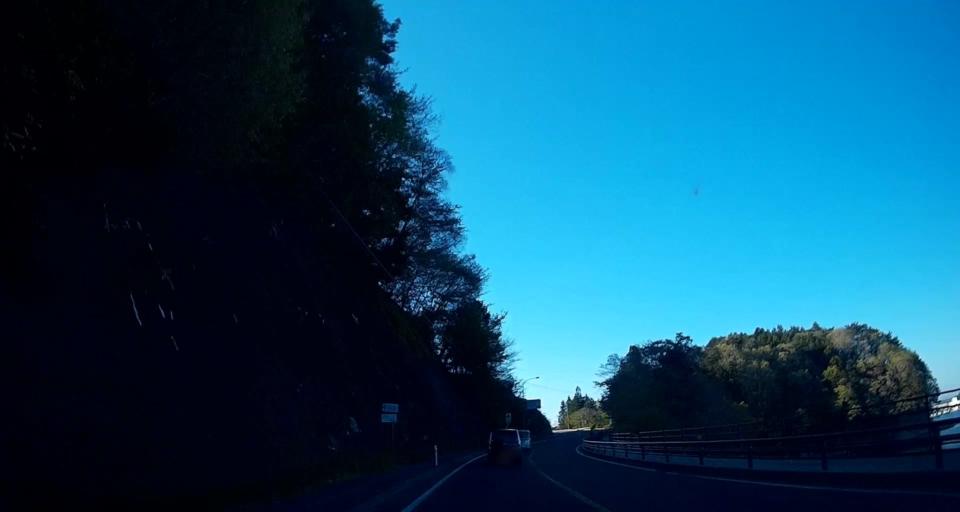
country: JP
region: Iwate
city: Miyako
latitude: 39.6141
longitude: 141.9618
